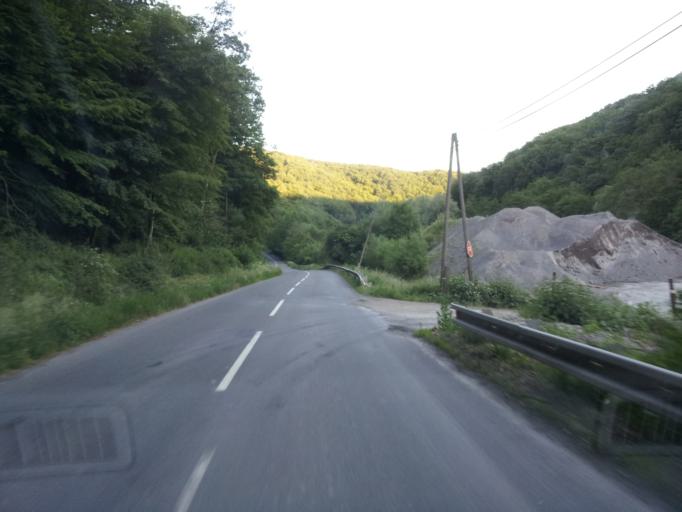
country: SK
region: Banskobystricky
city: Krupina
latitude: 48.3199
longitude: 18.9777
